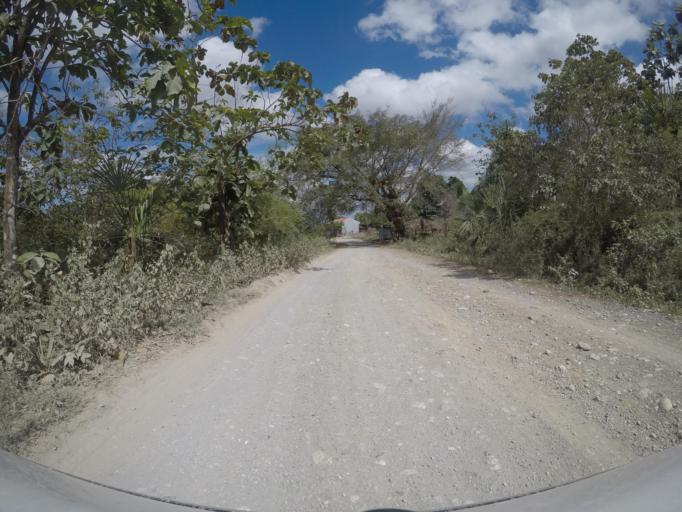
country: TL
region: Viqueque
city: Viqueque
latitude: -8.8664
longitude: 126.3340
